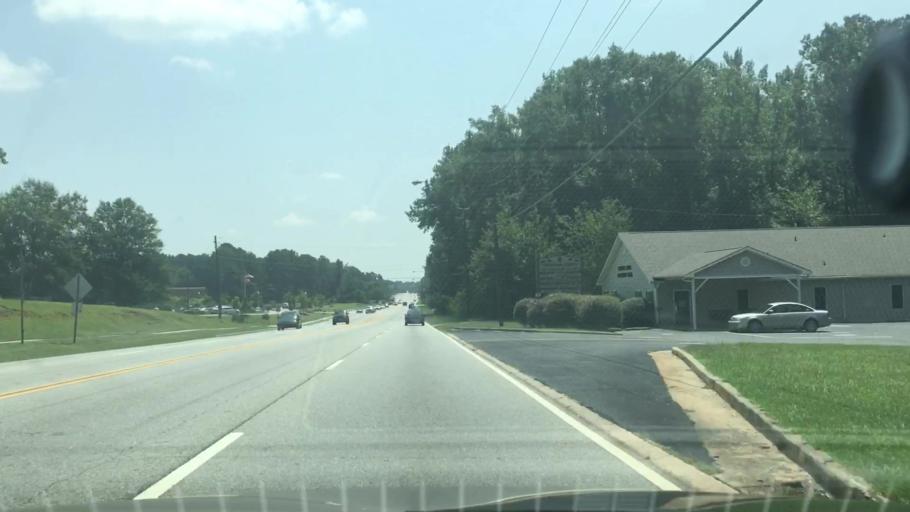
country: US
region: Georgia
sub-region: Spalding County
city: Griffin
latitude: 33.2442
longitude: -84.2516
